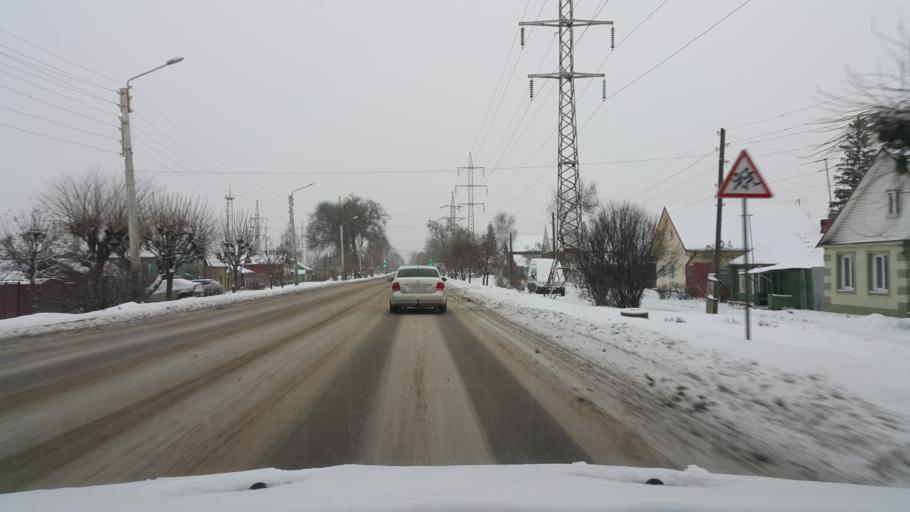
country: RU
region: Tambov
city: Pokrovo-Prigorodnoye
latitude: 52.7072
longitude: 41.4217
